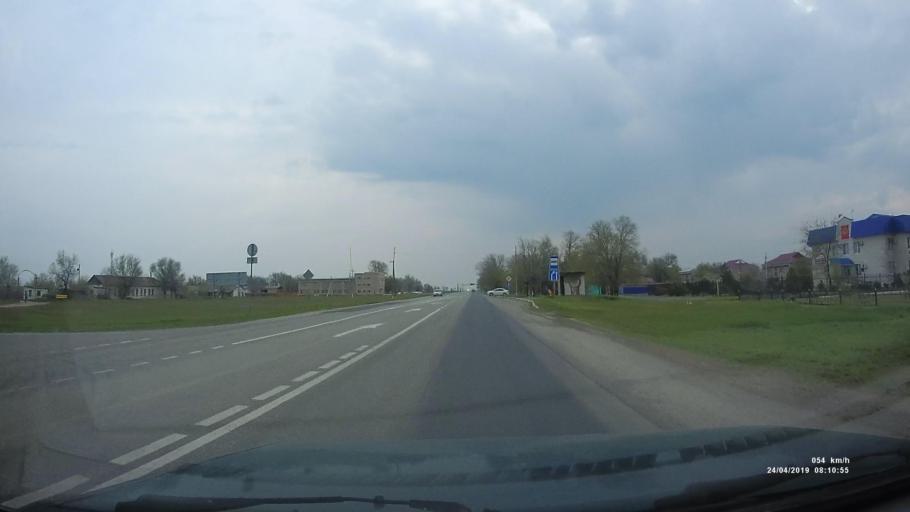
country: RU
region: Kalmykiya
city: Priyutnoye
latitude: 46.1004
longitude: 43.5220
